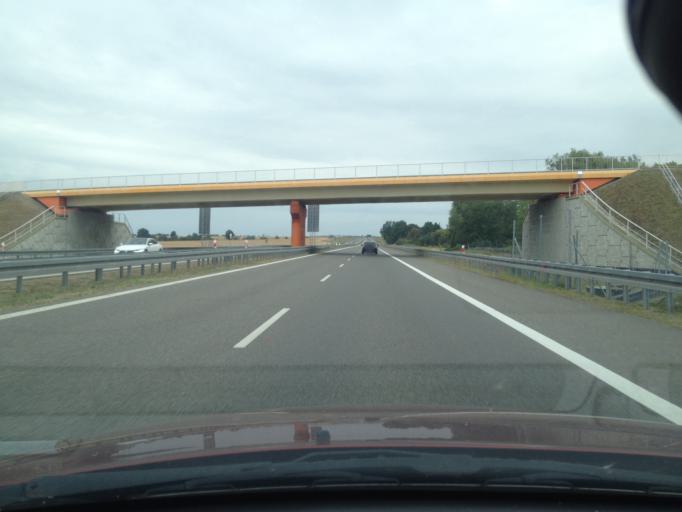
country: PL
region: Lubusz
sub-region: Powiat gorzowski
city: Jenin
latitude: 52.7805
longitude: 15.1223
